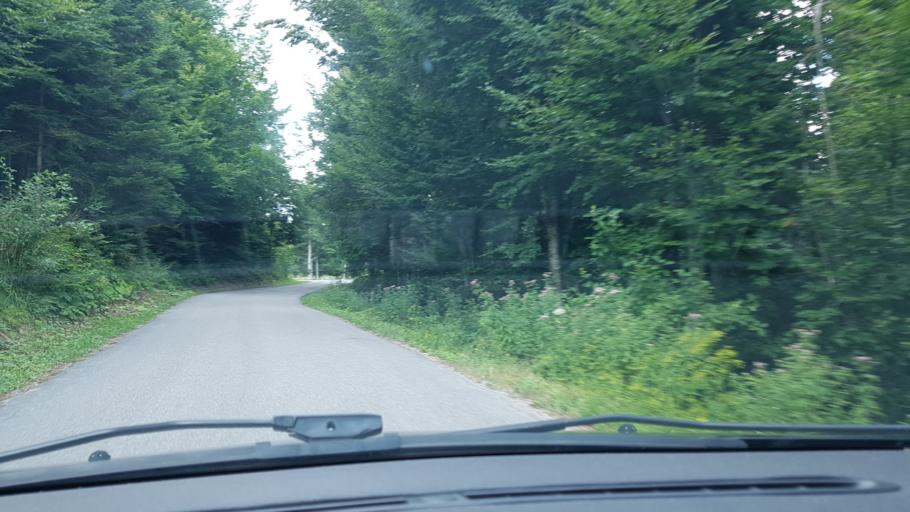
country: HR
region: Primorsko-Goranska
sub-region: Grad Delnice
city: Delnice
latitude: 45.3792
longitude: 14.7022
